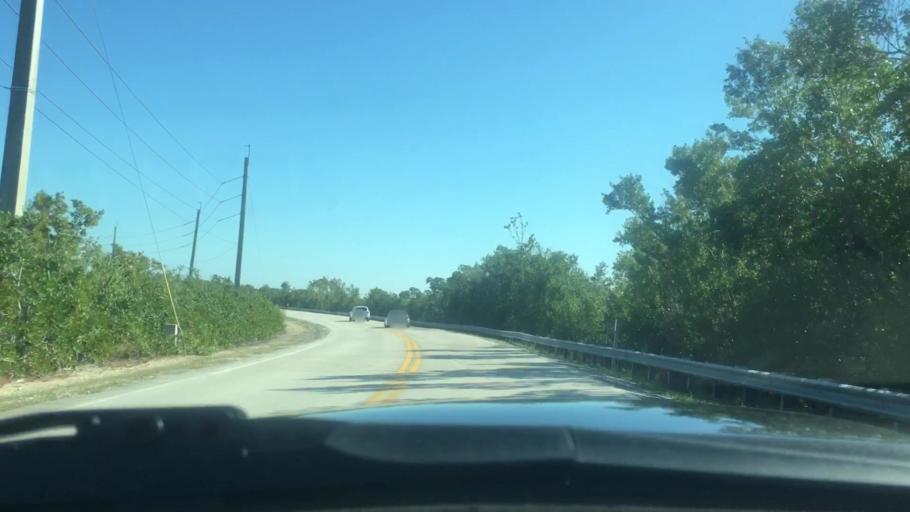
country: US
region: Florida
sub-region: Monroe County
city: North Key Largo
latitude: 25.2792
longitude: -80.3419
